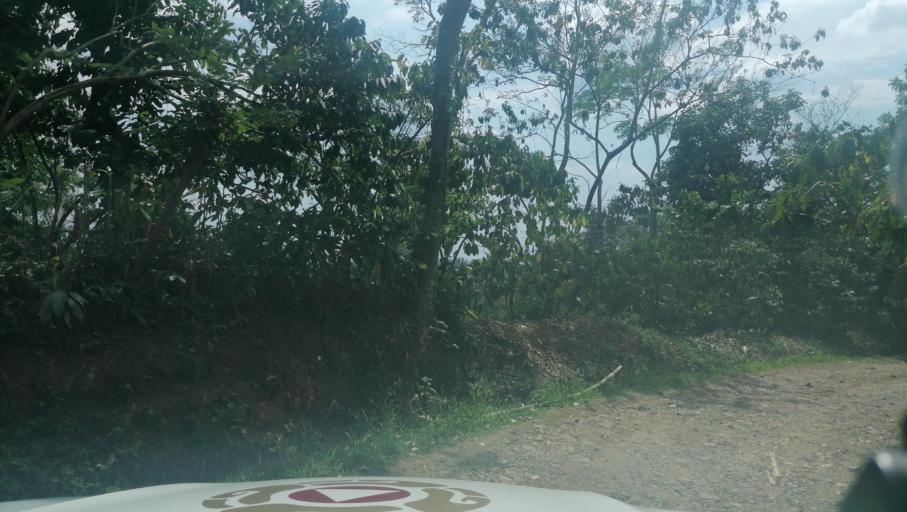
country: MX
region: Chiapas
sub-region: Cacahoatan
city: Benito Juarez
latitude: 15.0558
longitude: -92.2276
